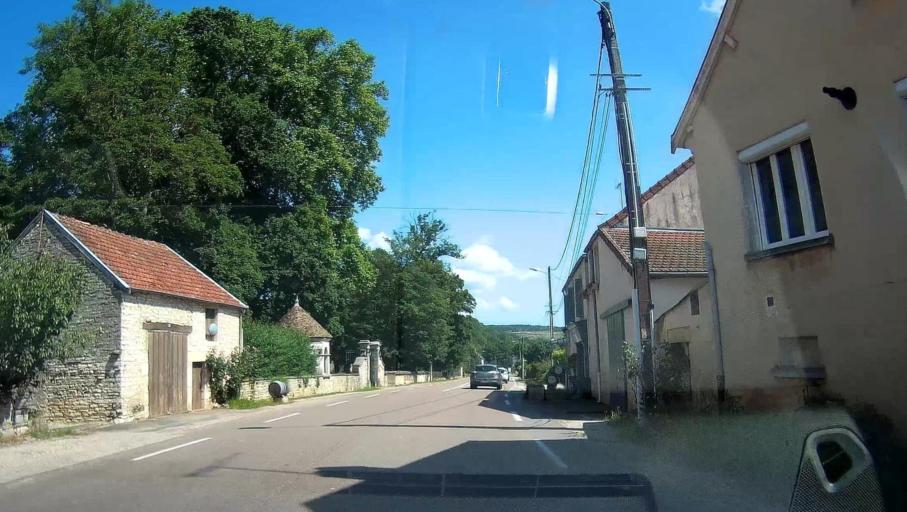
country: FR
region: Bourgogne
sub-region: Departement de la Cote-d'Or
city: Meursault
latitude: 46.9809
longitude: 4.7106
